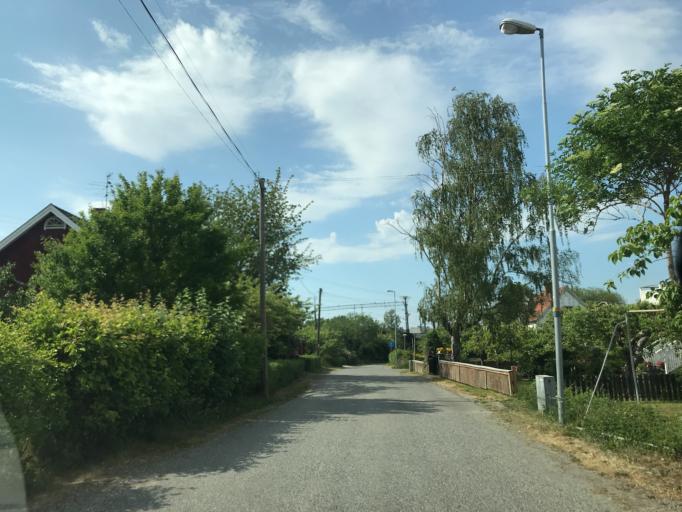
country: SE
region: Stockholm
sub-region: Sollentuna Kommun
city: Sollentuna
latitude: 59.4205
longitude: 17.9561
